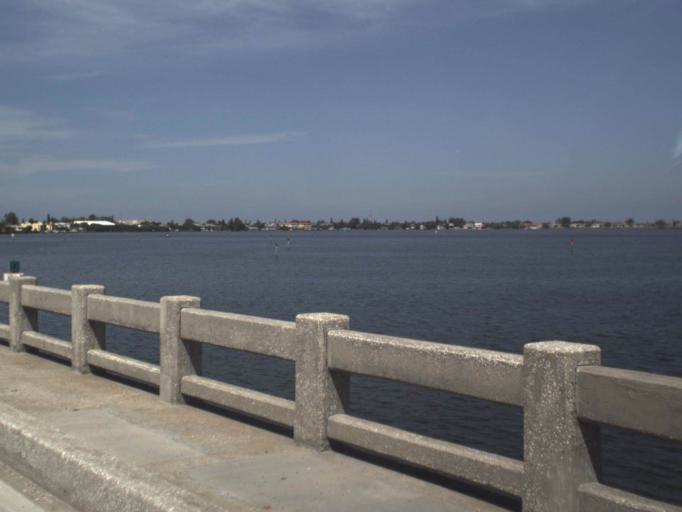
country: US
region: Florida
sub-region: Manatee County
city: Holmes Beach
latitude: 27.4970
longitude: -82.6985
